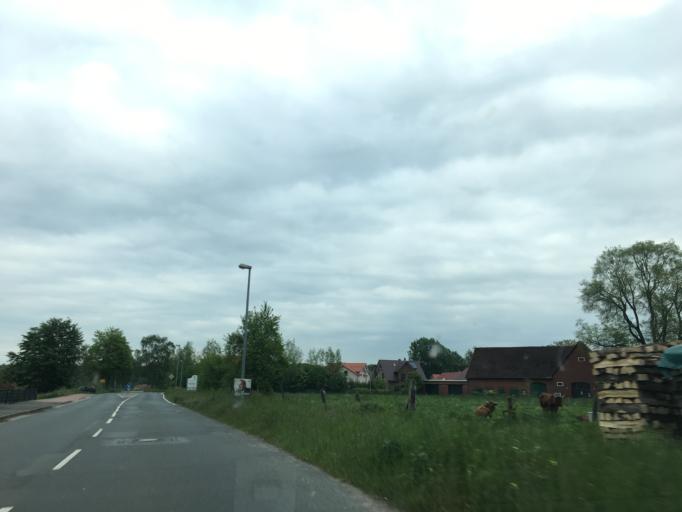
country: DE
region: Lower Saxony
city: Haste
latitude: 52.3804
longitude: 9.3957
